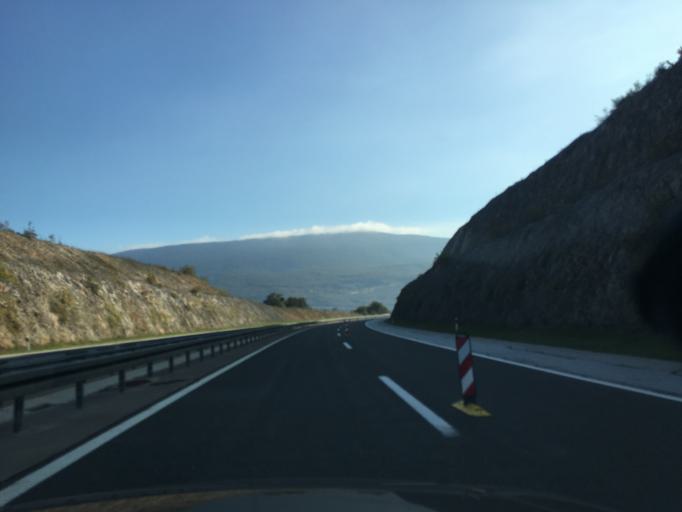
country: HR
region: Licko-Senjska
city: Brinje
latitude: 45.0514
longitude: 15.1834
